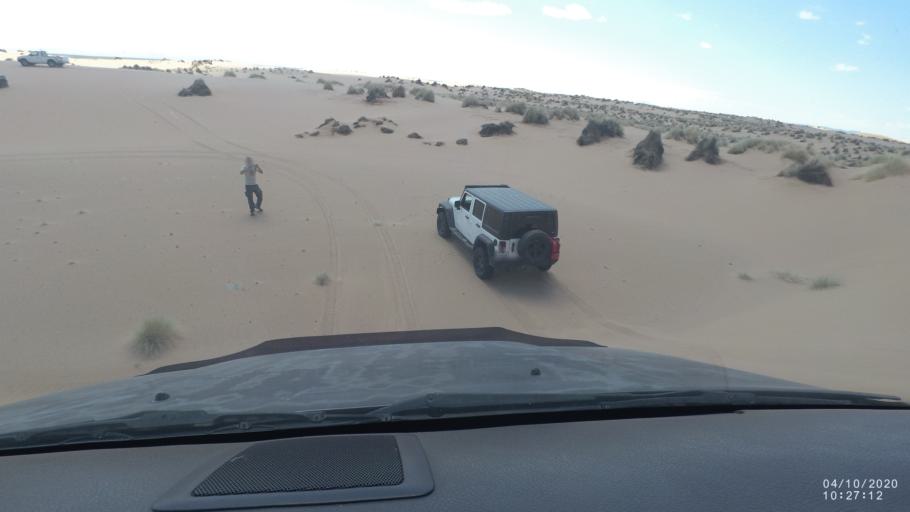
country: BO
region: Oruro
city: Poopo
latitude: -18.7040
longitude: -67.4870
